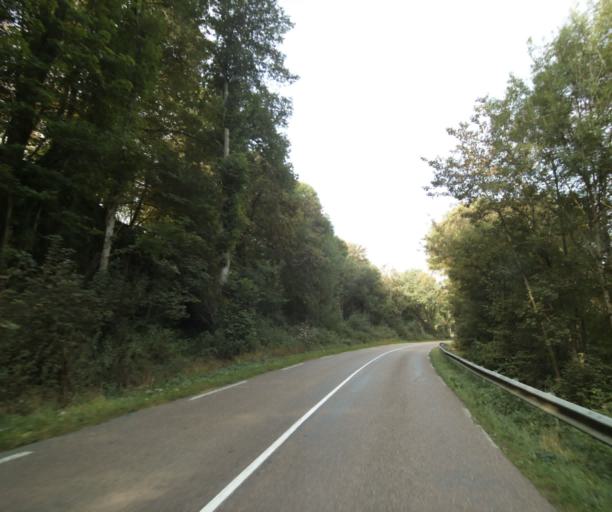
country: FR
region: Bourgogne
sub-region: Departement de Saone-et-Loire
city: Charolles
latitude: 46.4232
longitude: 4.2716
